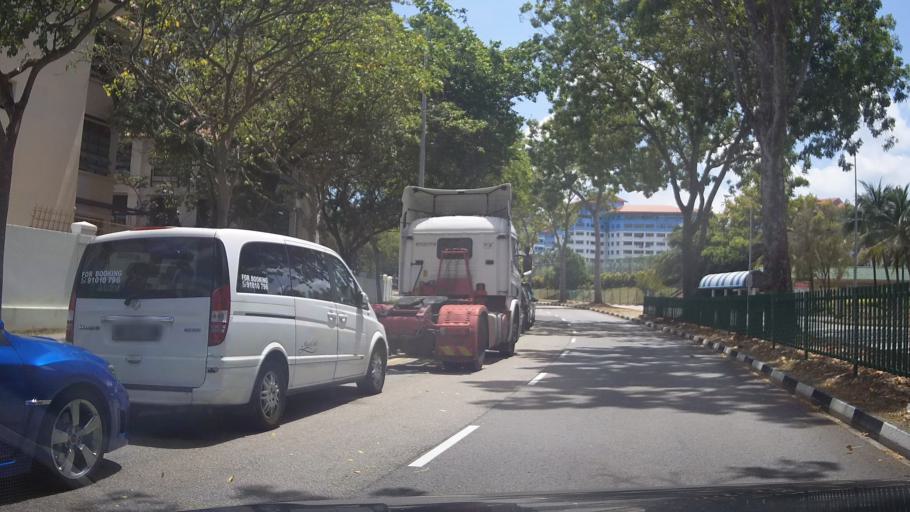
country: MY
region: Johor
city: Kampung Pasir Gudang Baru
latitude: 1.3711
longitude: 103.9637
